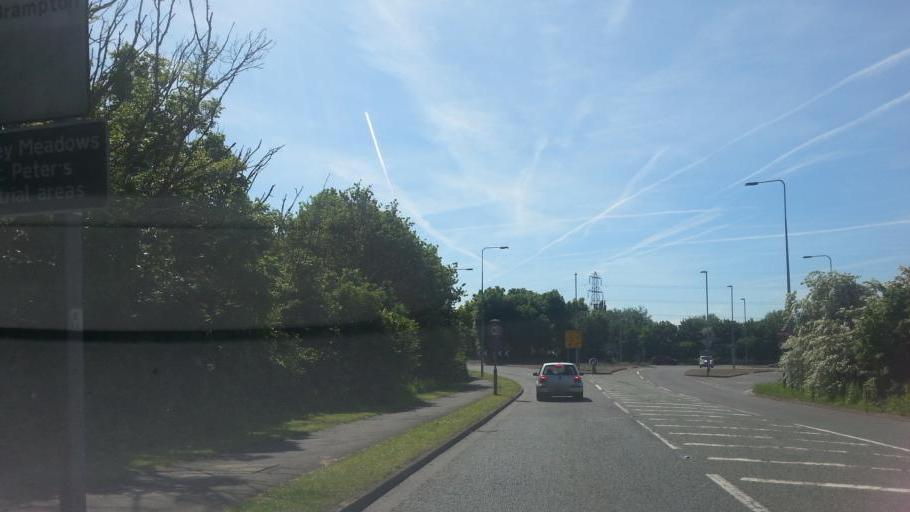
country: GB
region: England
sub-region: Cambridgeshire
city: Huntingdon
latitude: 52.3441
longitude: -0.1980
